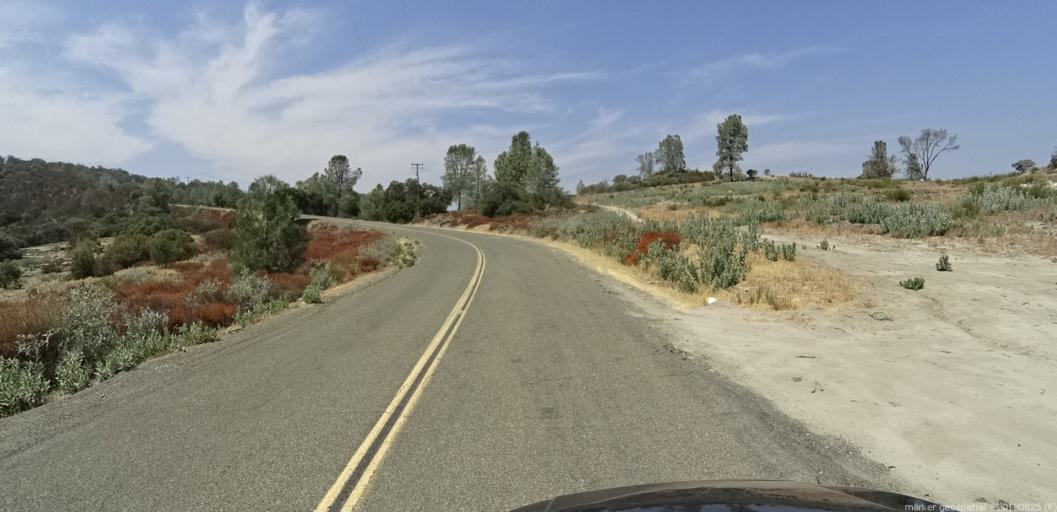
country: US
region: California
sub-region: San Luis Obispo County
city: San Miguel
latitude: 35.9210
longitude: -120.5232
